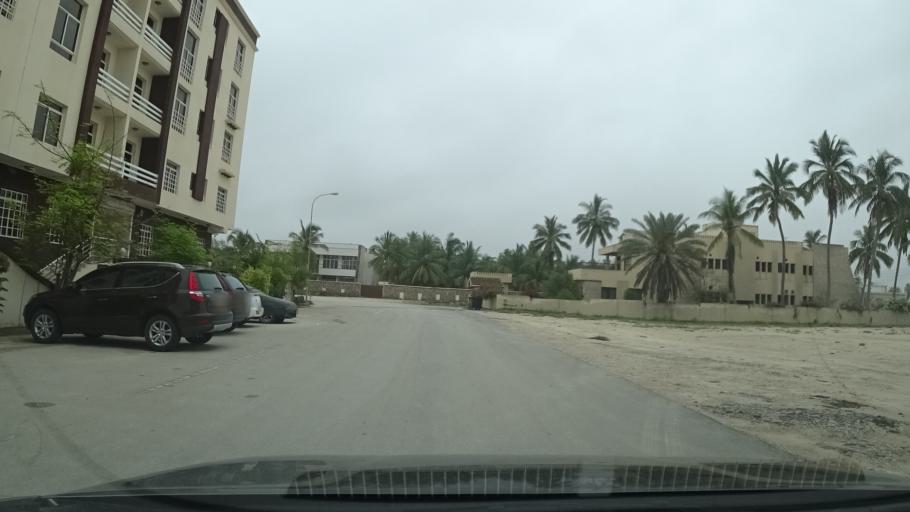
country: OM
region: Zufar
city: Salalah
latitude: 17.0100
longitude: 54.1568
